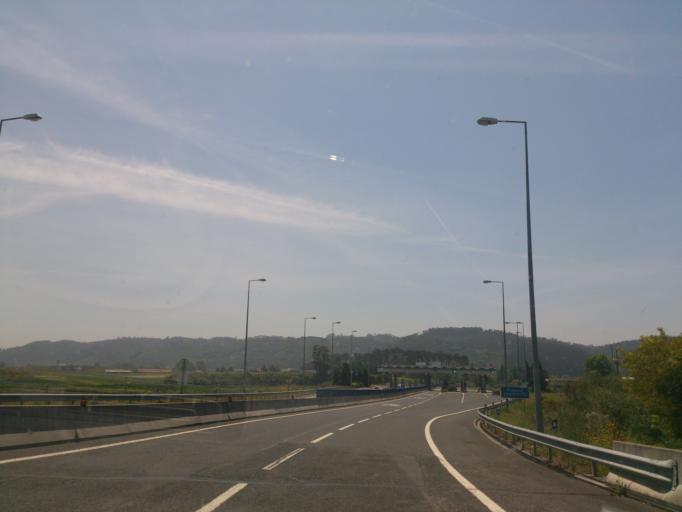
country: PT
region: Leiria
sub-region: Alcobaca
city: Alcobaca
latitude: 39.5861
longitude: -9.0088
